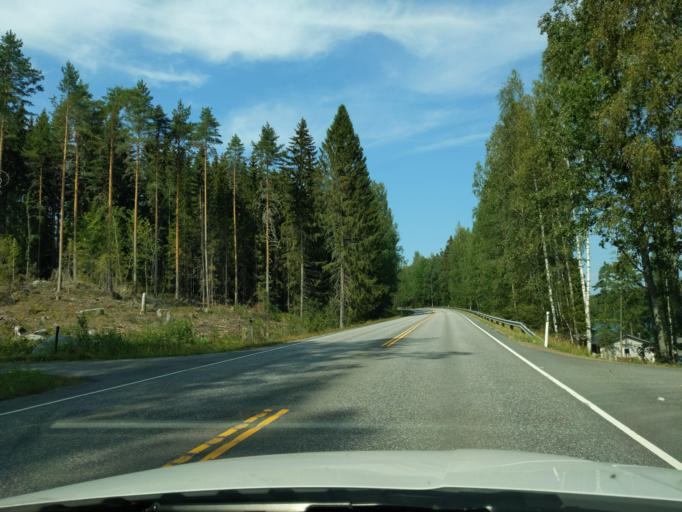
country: FI
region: Paijanne Tavastia
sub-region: Lahti
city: Padasjoki
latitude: 61.4024
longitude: 25.1816
